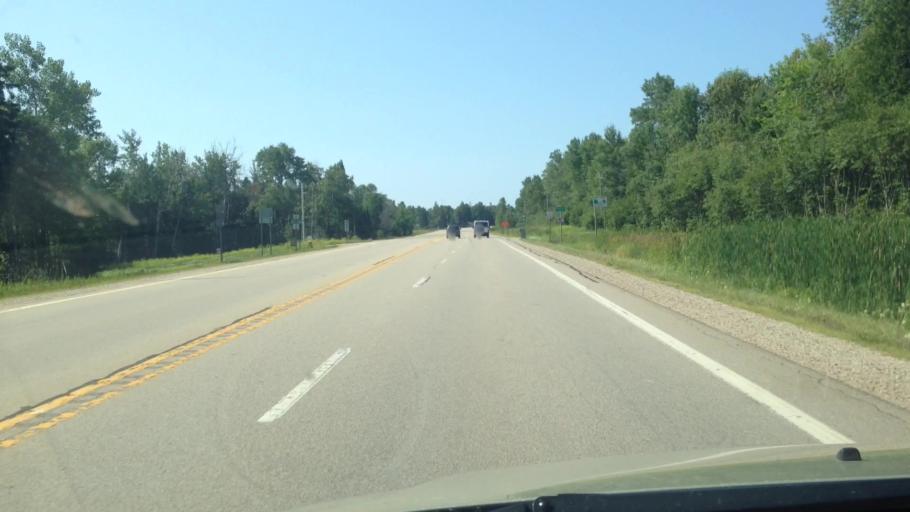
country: US
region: Michigan
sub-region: Delta County
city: Escanaba
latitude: 45.5517
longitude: -87.2698
